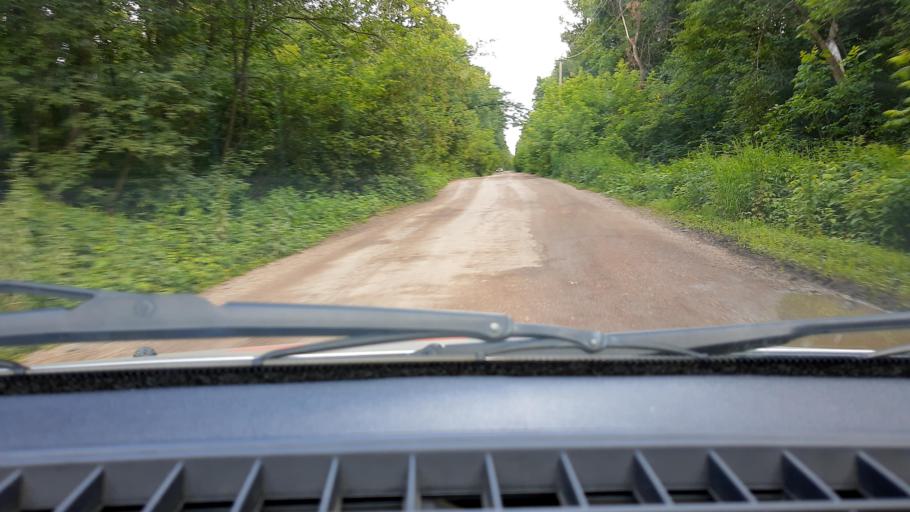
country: RU
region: Bashkortostan
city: Ufa
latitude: 54.6862
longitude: 56.0545
